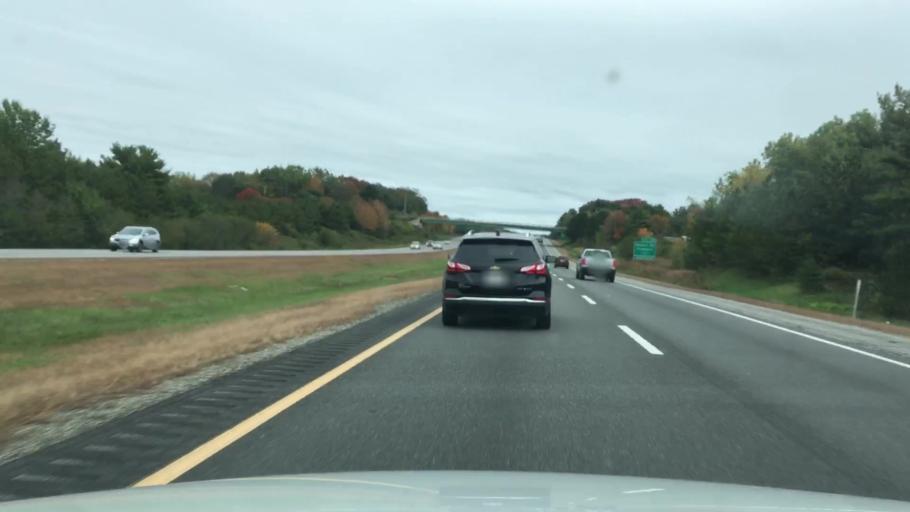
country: US
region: Maine
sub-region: Cumberland County
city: Freeport
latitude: 43.8265
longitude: -70.1375
